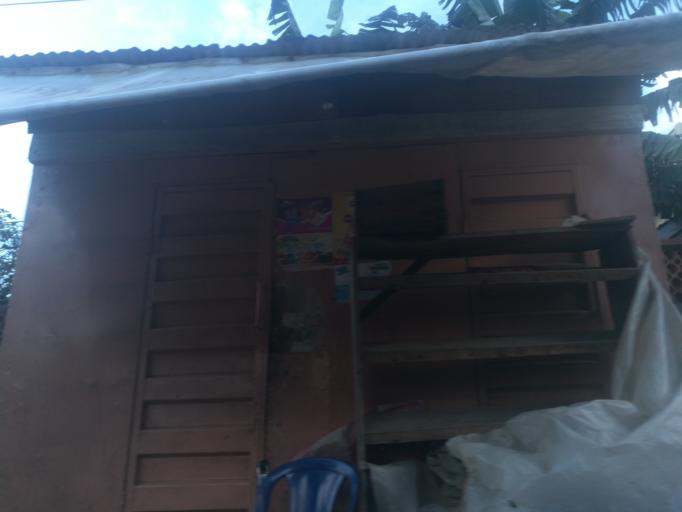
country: NG
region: Lagos
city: Ojota
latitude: 6.5639
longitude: 3.3775
